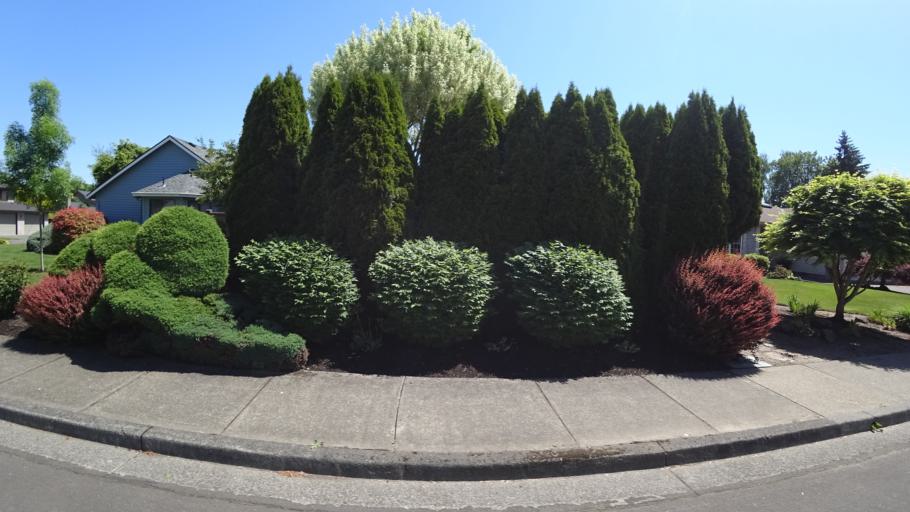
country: US
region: Oregon
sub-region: Washington County
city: Rockcreek
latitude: 45.5373
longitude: -122.9236
